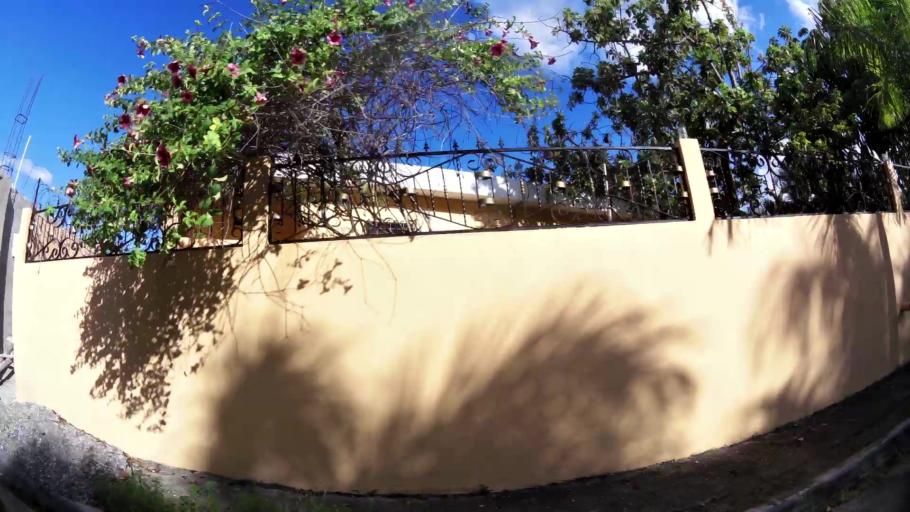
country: DO
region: Nacional
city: Santo Domingo
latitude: 18.5112
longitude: -69.9776
